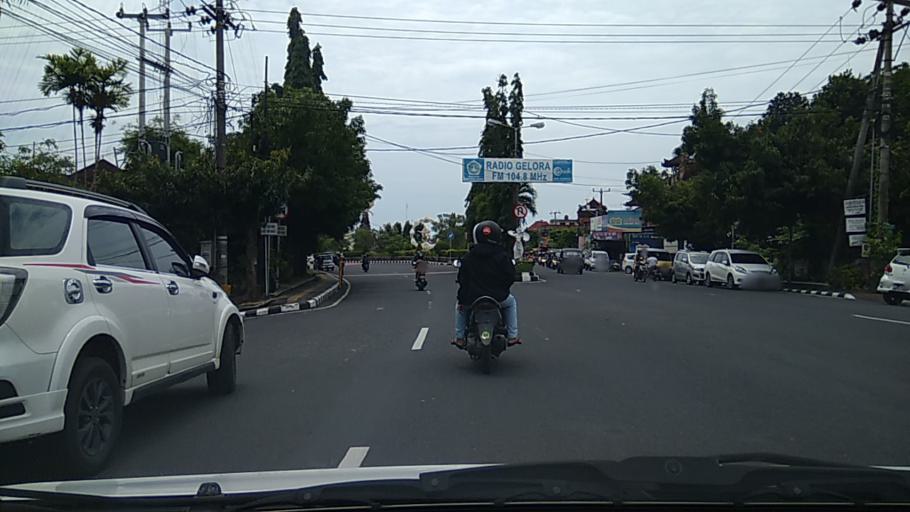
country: ID
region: Bali
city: Banjar Kelodan
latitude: -8.5397
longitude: 115.3226
